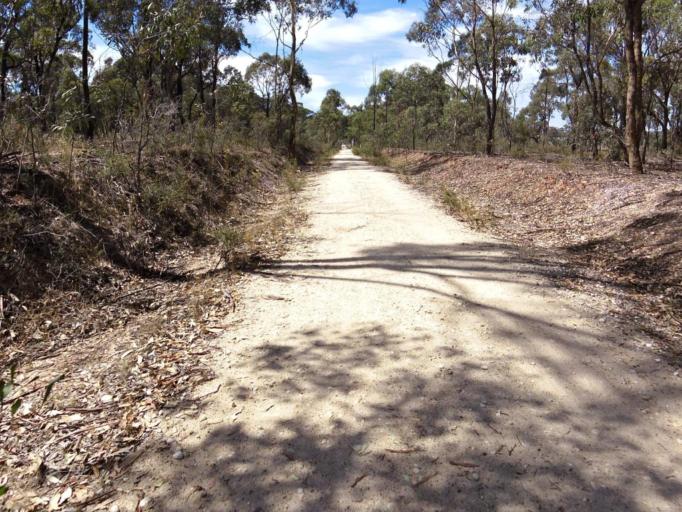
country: AU
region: Victoria
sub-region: Greater Bendigo
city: White Hills
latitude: -36.7588
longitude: 144.3333
